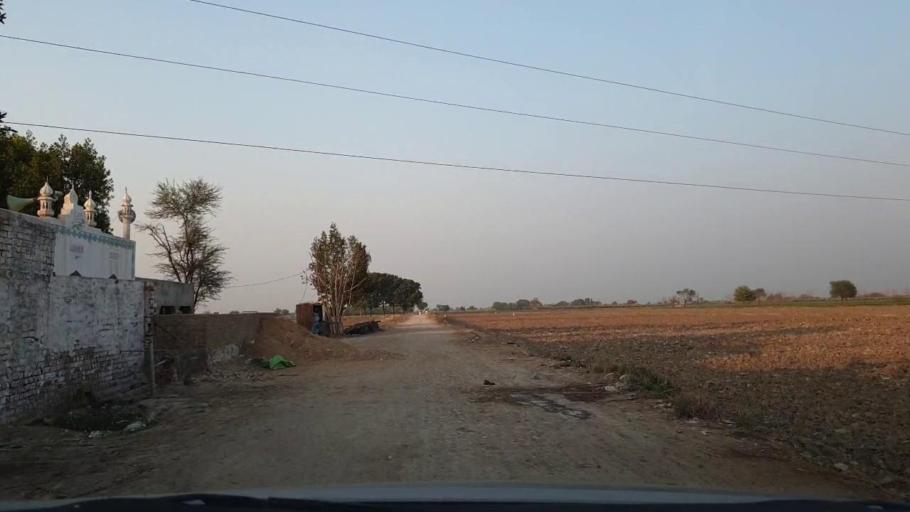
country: PK
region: Sindh
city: Tando Adam
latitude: 25.7127
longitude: 68.5792
